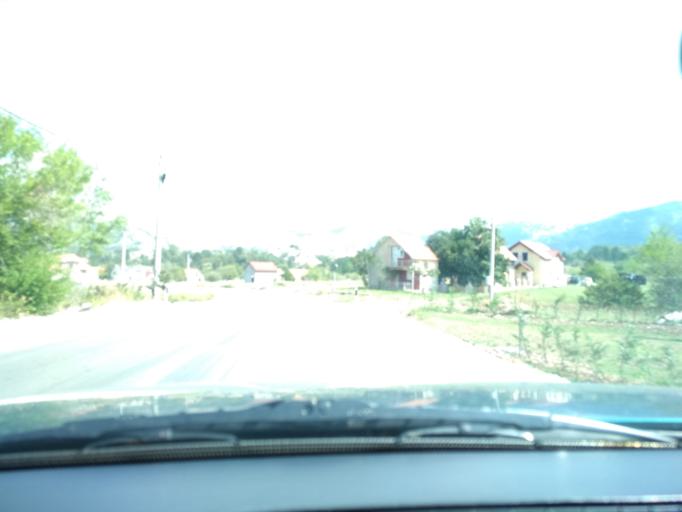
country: ME
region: Kotor
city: Kotor
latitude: 42.4275
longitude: 18.8034
